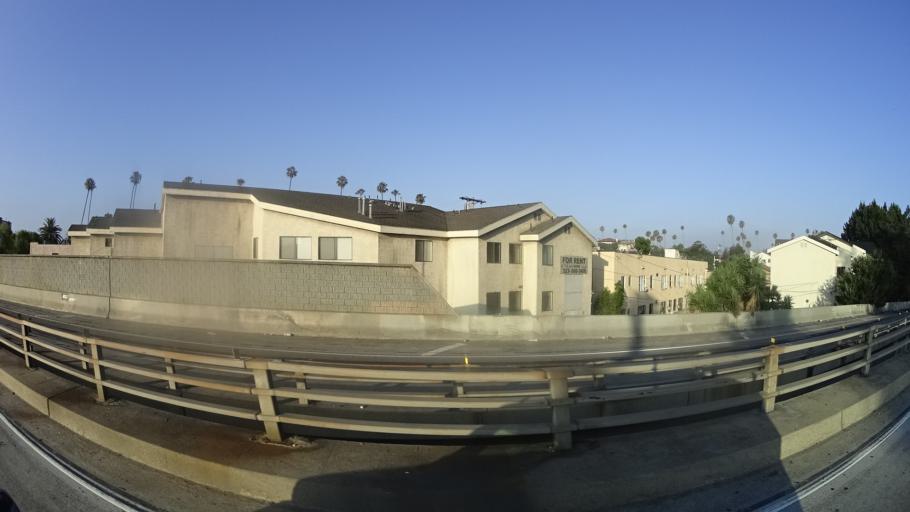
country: US
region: California
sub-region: Los Angeles County
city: Silver Lake
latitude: 34.0823
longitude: -118.2973
